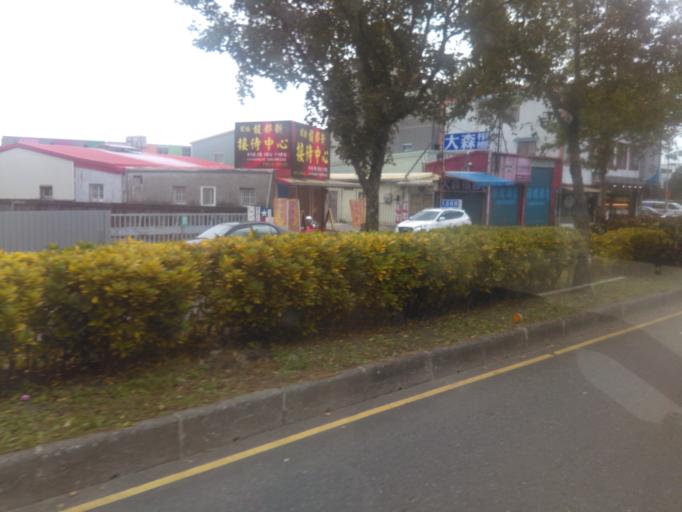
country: TW
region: Taiwan
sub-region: Yilan
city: Yilan
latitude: 24.8371
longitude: 121.7873
